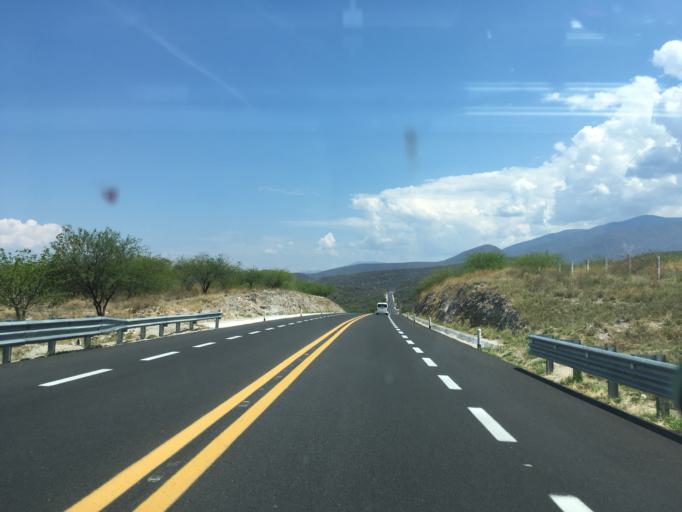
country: MX
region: Puebla
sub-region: San Jose Miahuatlan
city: San Pedro Tetitlan
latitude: 18.2054
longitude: -97.2818
